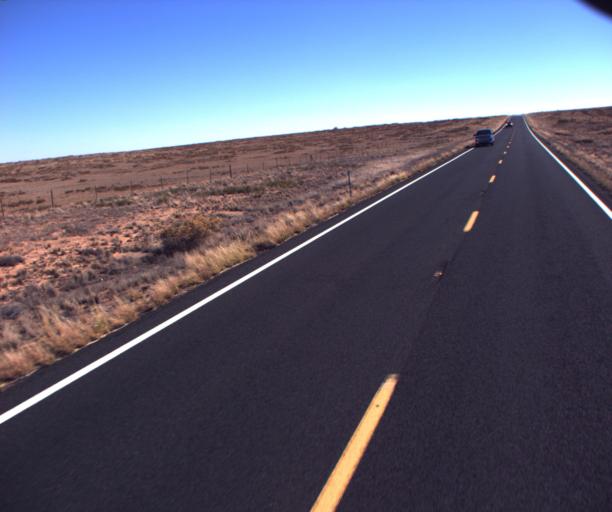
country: US
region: Arizona
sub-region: Coconino County
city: Tuba City
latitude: 36.0136
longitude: -111.0847
